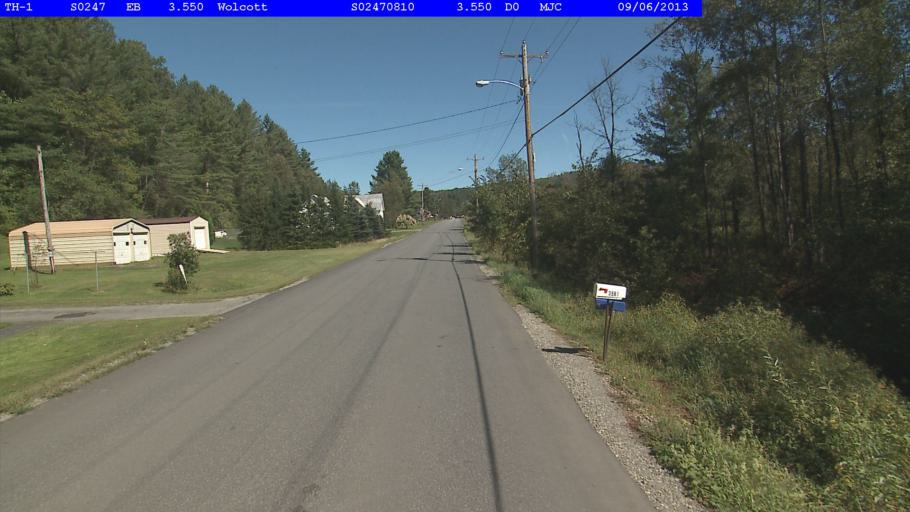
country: US
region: Vermont
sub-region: Lamoille County
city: Morrisville
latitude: 44.6045
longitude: -72.4658
